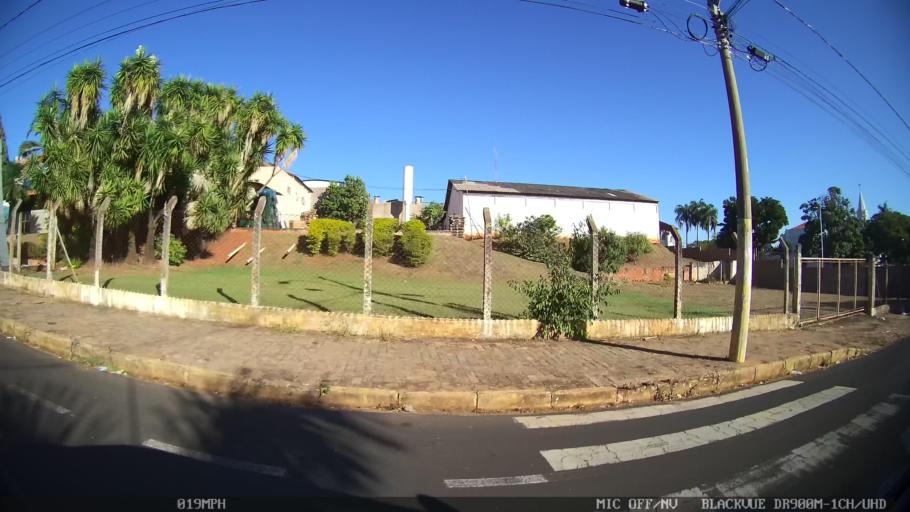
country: BR
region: Sao Paulo
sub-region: Olimpia
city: Olimpia
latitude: -20.7364
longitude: -48.9082
